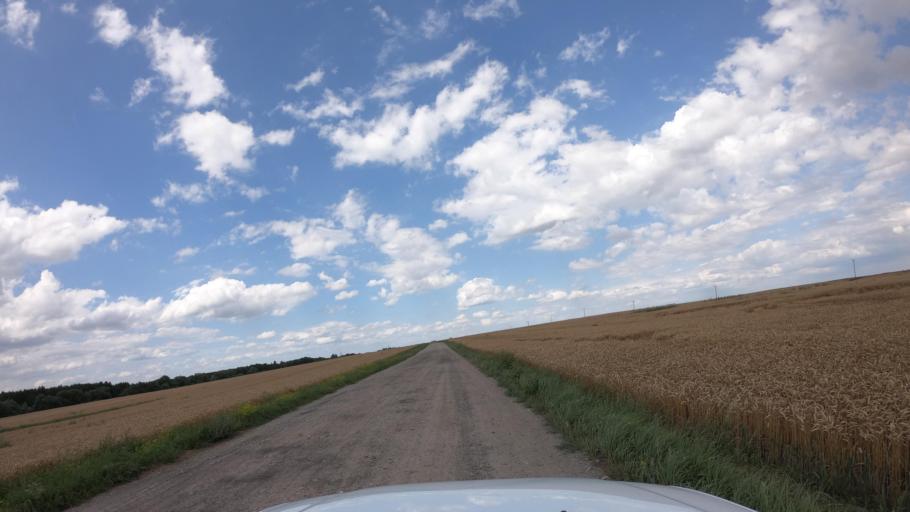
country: PL
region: West Pomeranian Voivodeship
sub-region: Powiat pyrzycki
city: Warnice
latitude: 53.2544
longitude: 14.9113
